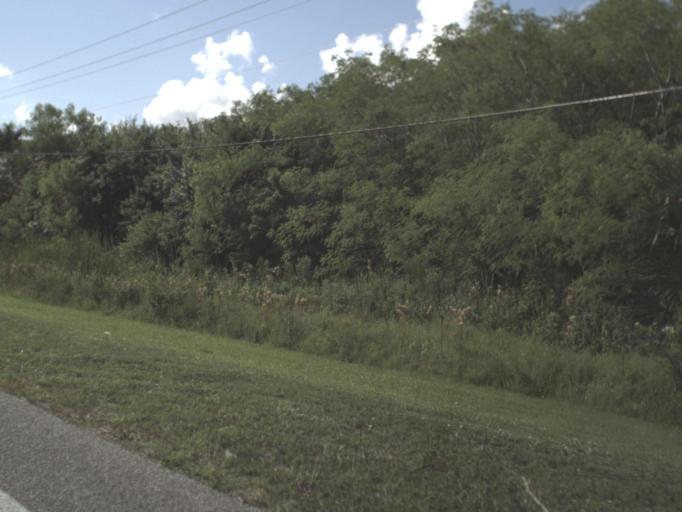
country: US
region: Florida
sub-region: Charlotte County
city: Charlotte Park
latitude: 26.9048
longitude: -82.0368
